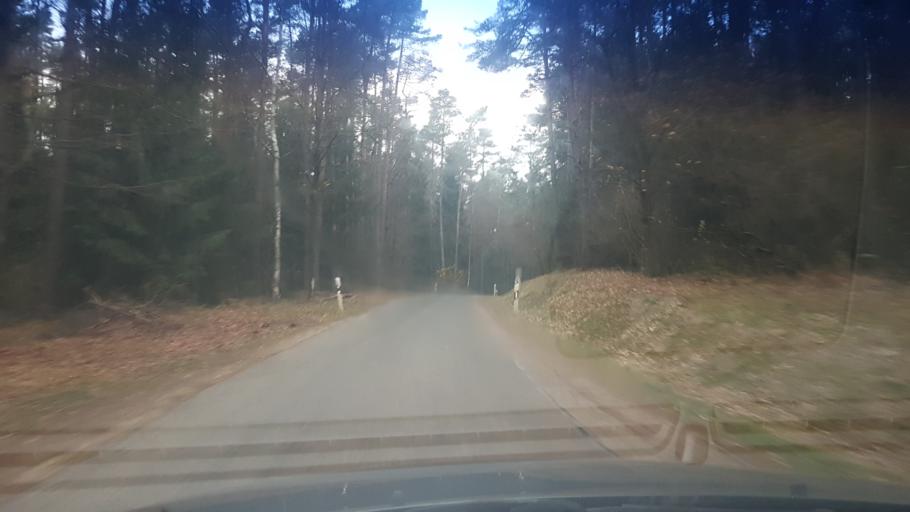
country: DE
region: Bavaria
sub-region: Upper Franconia
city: Weismain
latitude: 50.0469
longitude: 11.2858
